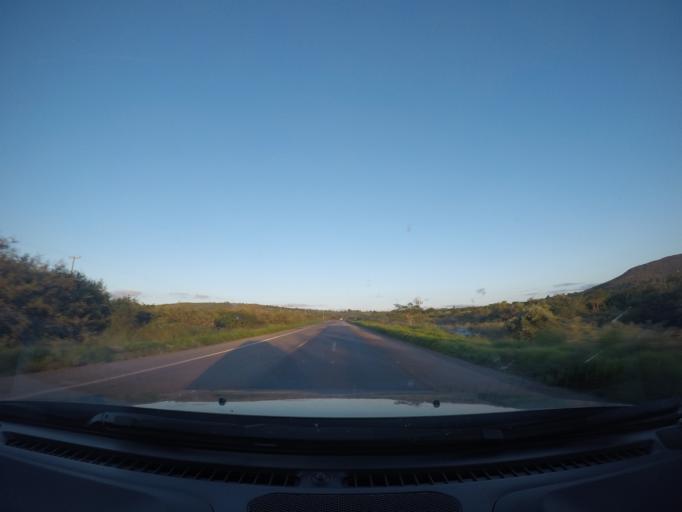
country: BR
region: Bahia
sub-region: Seabra
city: Seabra
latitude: -12.3892
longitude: -41.8929
